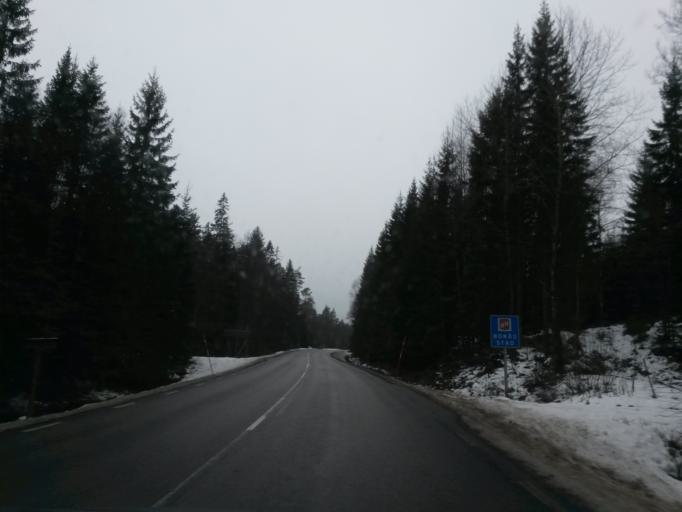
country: SE
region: Vaestra Goetaland
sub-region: Tranemo Kommun
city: Langhem
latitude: 57.6970
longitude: 13.2657
